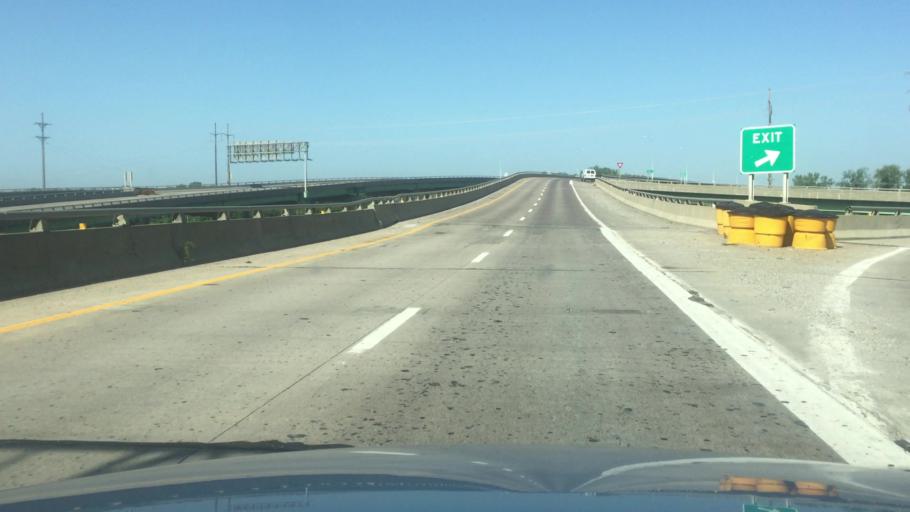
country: US
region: Kansas
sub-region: Doniphan County
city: Elwood
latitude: 39.7487
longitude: -94.8547
